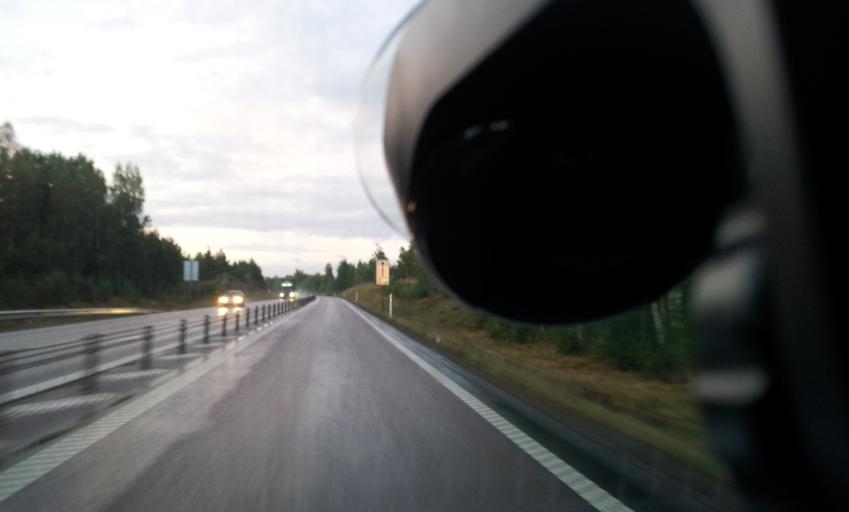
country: SE
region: Kalmar
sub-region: Oskarshamns Kommun
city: Oskarshamn
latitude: 57.2203
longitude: 16.4355
